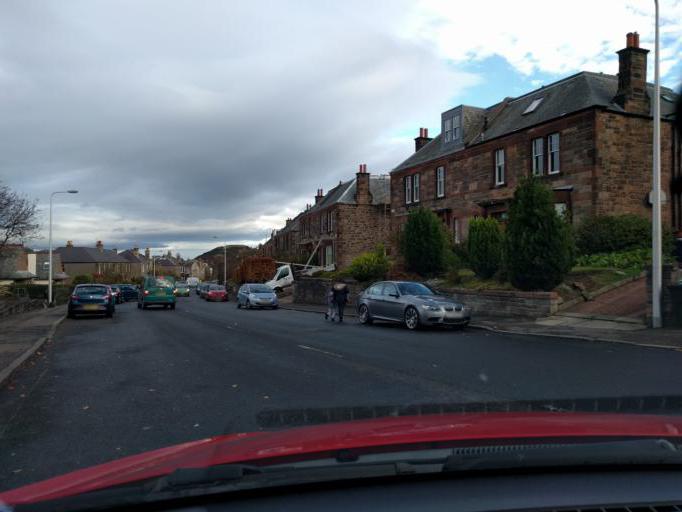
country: GB
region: Scotland
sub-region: Edinburgh
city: Edinburgh
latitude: 55.9187
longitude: -3.2157
